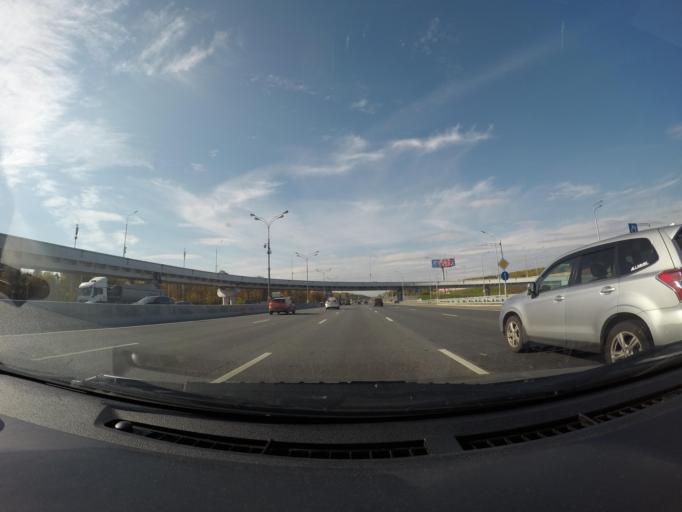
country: RU
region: Moscow
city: Vatutino
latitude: 55.8954
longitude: 37.6722
